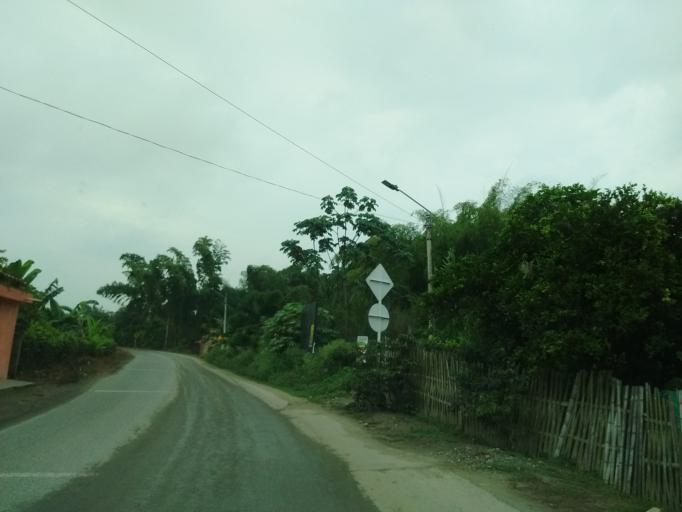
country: CO
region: Cauca
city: Padilla
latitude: 3.2282
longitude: -76.3146
